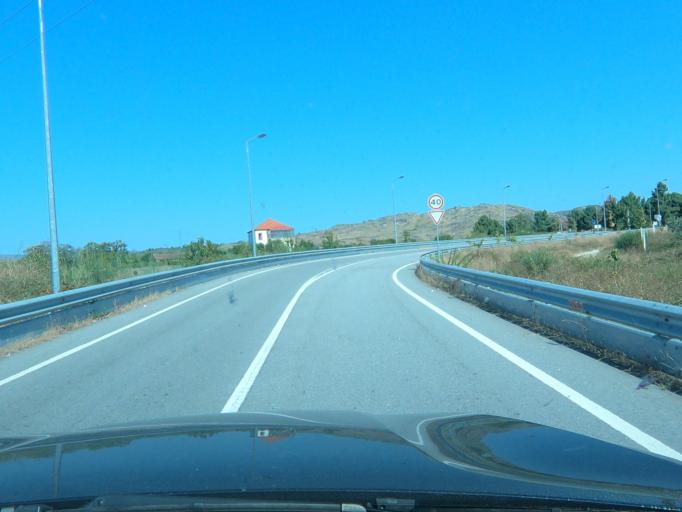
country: PT
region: Vila Real
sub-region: Sabrosa
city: Vilela
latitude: 41.2673
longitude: -7.6345
